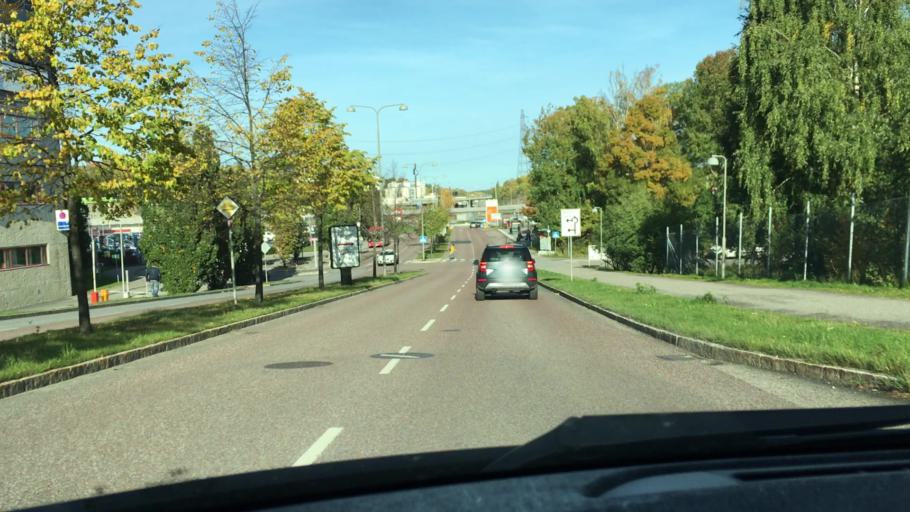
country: SE
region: Stockholm
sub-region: Huddinge Kommun
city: Segeltorp
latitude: 59.2668
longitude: 17.9121
